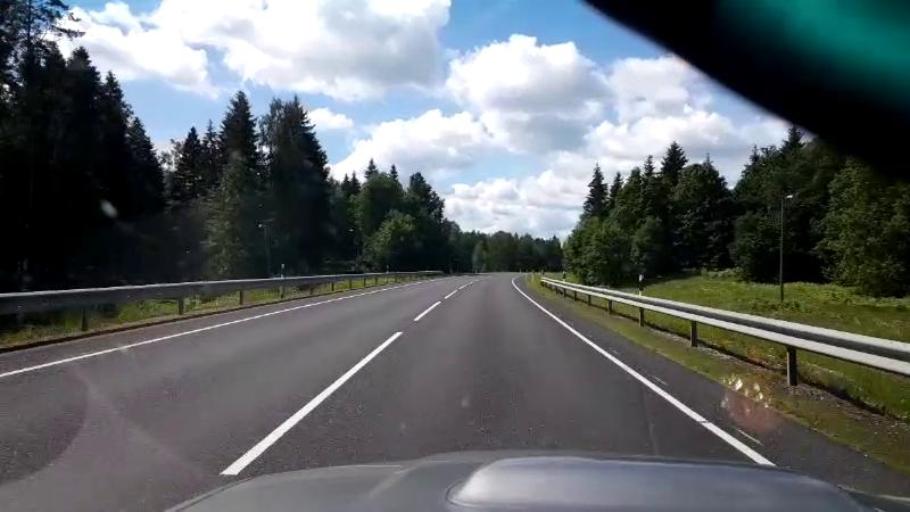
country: EE
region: Jaervamaa
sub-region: Jaerva-Jaani vald
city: Jarva-Jaani
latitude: 59.1299
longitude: 25.7504
